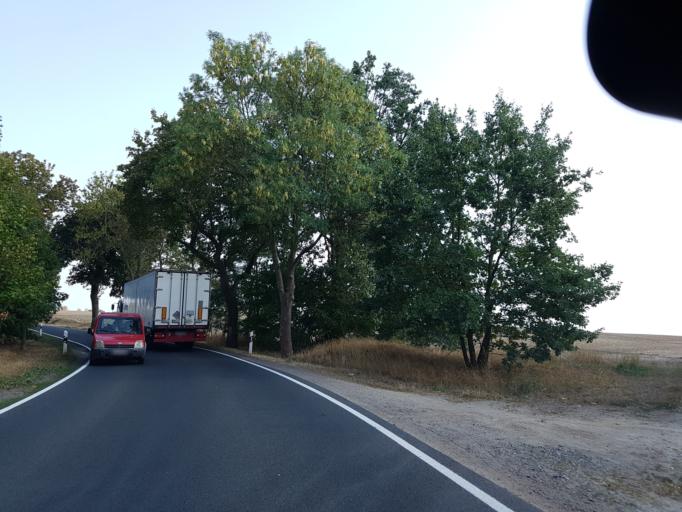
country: DE
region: Saxony-Anhalt
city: Pretzsch
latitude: 51.7070
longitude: 12.8090
